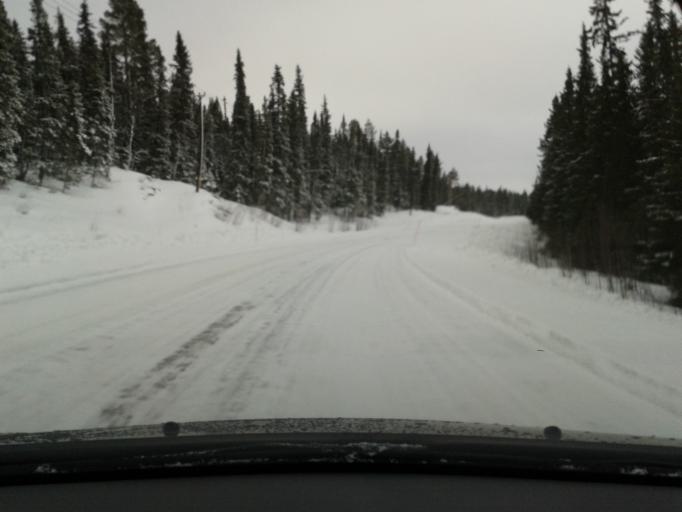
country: SE
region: Vaesterbotten
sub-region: Vilhelmina Kommun
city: Sjoberg
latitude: 65.2285
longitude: 15.9070
